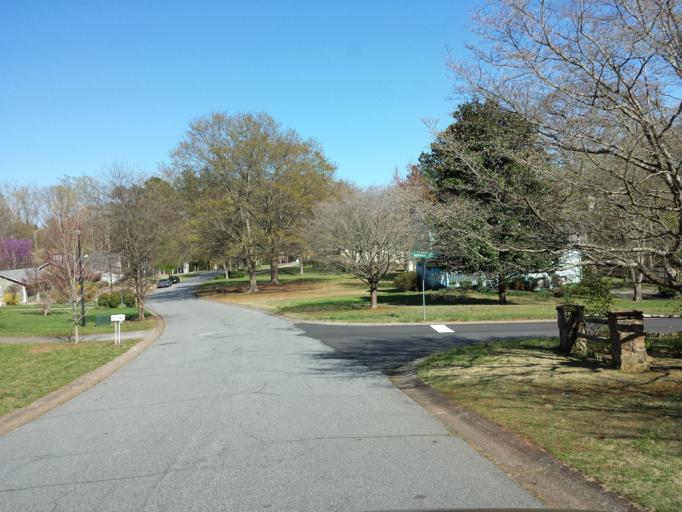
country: US
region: Georgia
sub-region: Cobb County
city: Marietta
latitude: 33.9547
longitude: -84.5720
